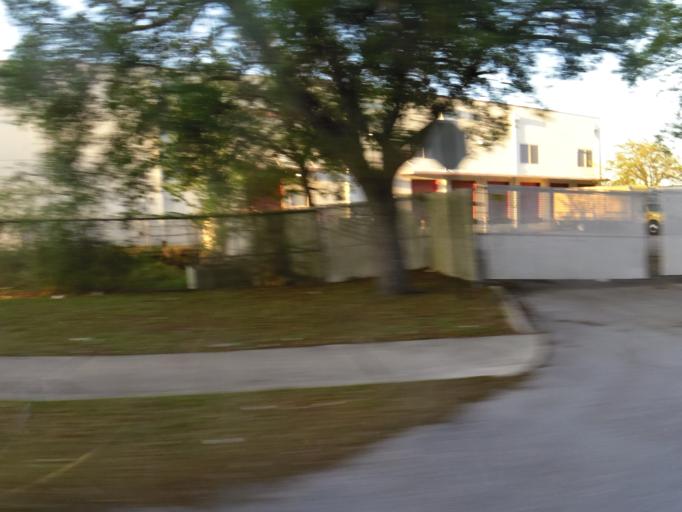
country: US
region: Florida
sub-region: Duval County
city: Jacksonville
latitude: 30.2883
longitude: -81.5839
